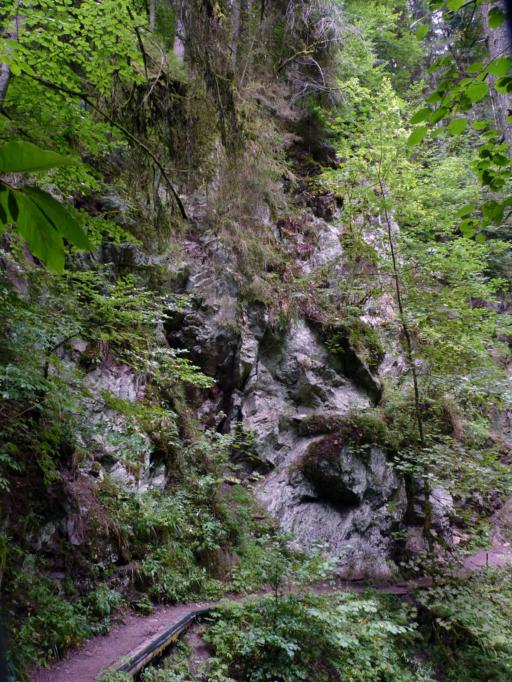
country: DE
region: Baden-Wuerttemberg
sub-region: Freiburg Region
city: Bonndorf im Schwarzwald
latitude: 47.8415
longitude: 8.3158
